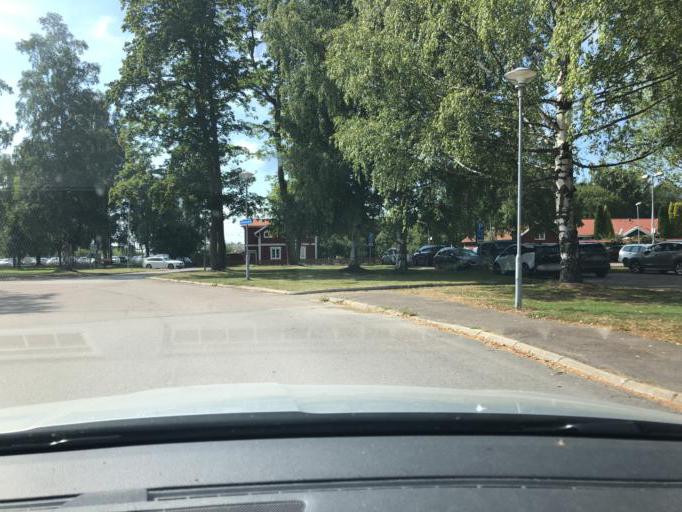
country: SE
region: Dalarna
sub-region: Avesta Kommun
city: Avesta
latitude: 60.1424
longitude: 16.2000
